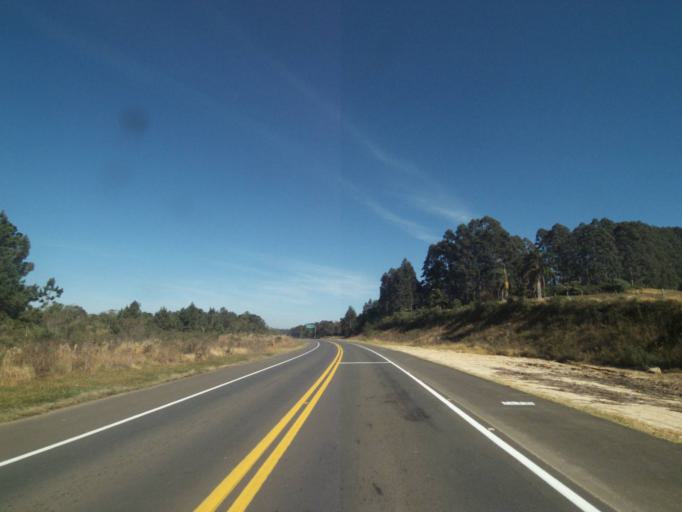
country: BR
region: Parana
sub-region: Tibagi
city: Tibagi
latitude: -24.8097
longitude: -50.4814
